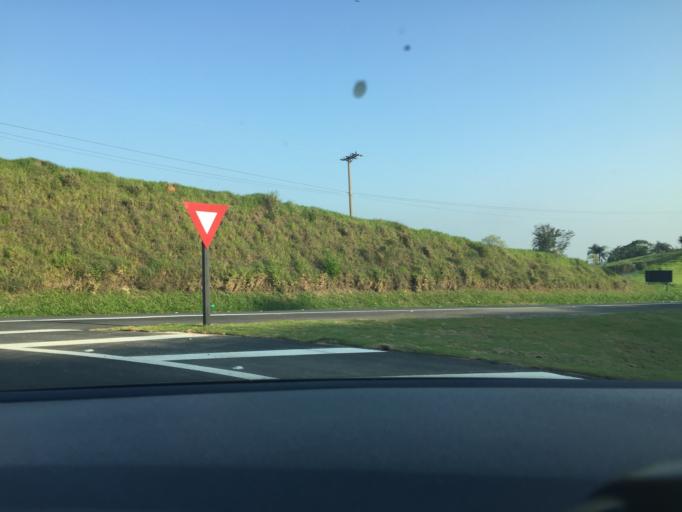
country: BR
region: Sao Paulo
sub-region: Louveira
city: Louveira
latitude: -23.0754
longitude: -46.9078
